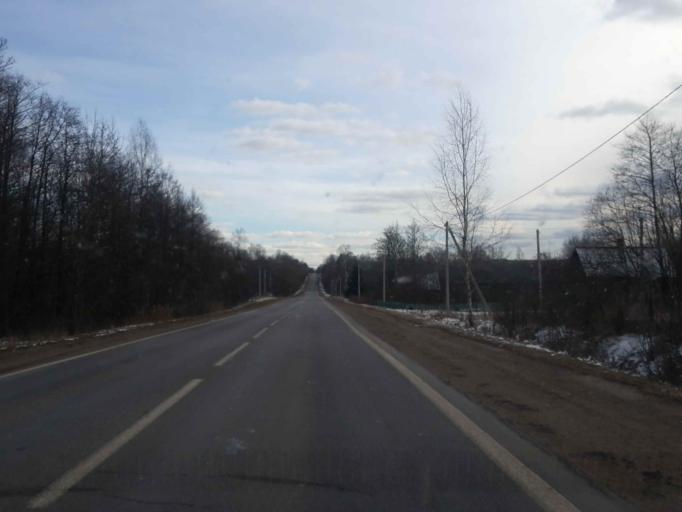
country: BY
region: Vitebsk
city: Pastavy
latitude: 54.9999
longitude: 26.8837
